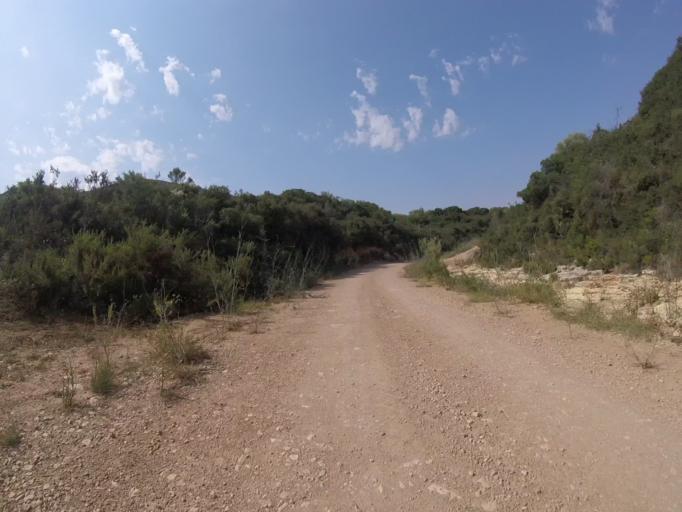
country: ES
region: Valencia
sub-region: Provincia de Castello
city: Alcala de Xivert
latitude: 40.3165
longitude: 0.1845
